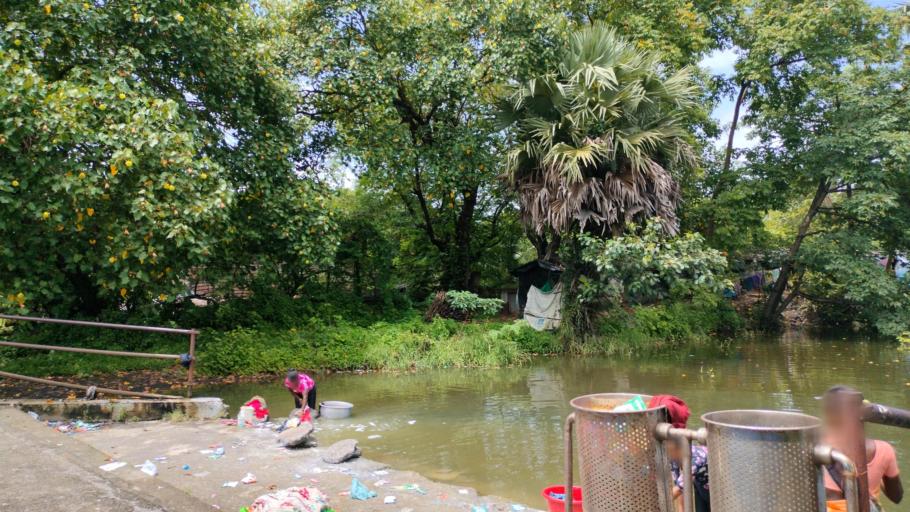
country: IN
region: Maharashtra
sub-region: Mumbai Suburban
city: Borivli
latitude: 19.2402
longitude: 72.7843
